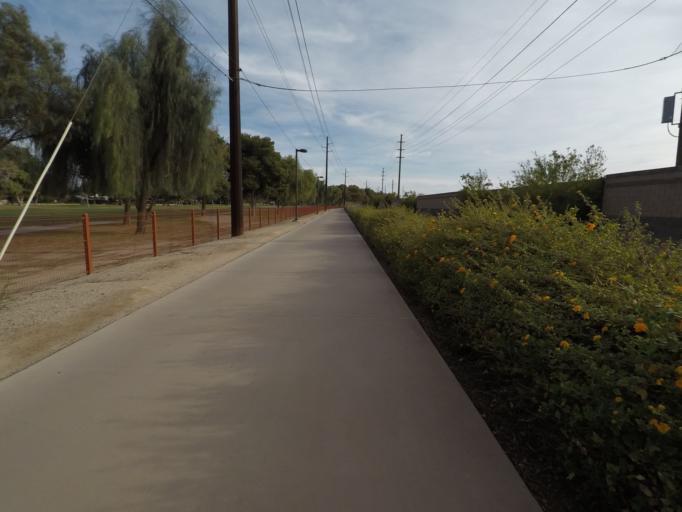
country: US
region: Arizona
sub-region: Maricopa County
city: Guadalupe
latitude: 33.3523
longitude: -111.9381
